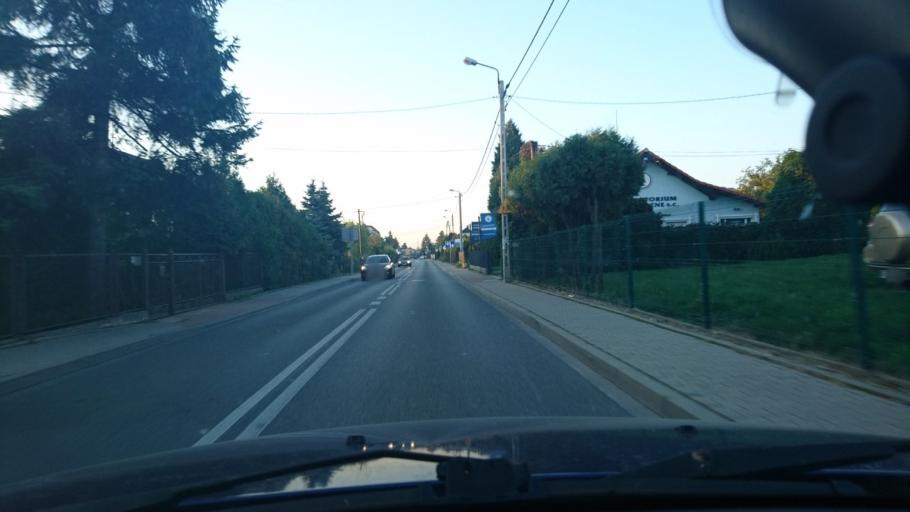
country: PL
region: Silesian Voivodeship
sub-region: Bielsko-Biala
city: Bielsko-Biala
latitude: 49.8519
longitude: 19.0500
